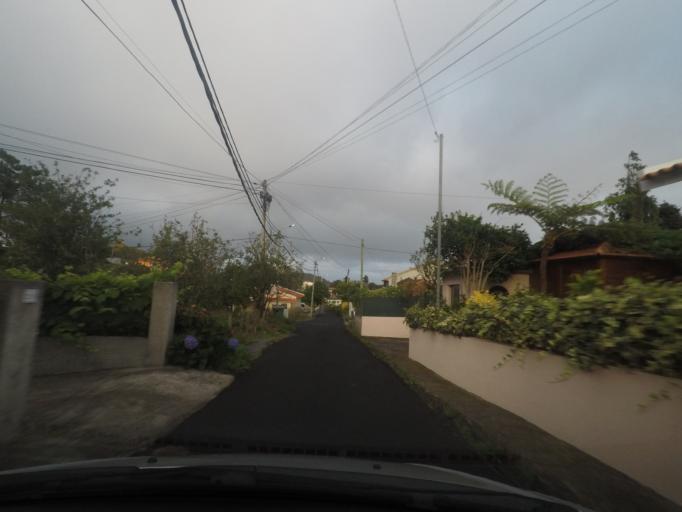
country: PT
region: Madeira
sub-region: Santa Cruz
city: Camacha
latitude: 32.6798
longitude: -16.8499
